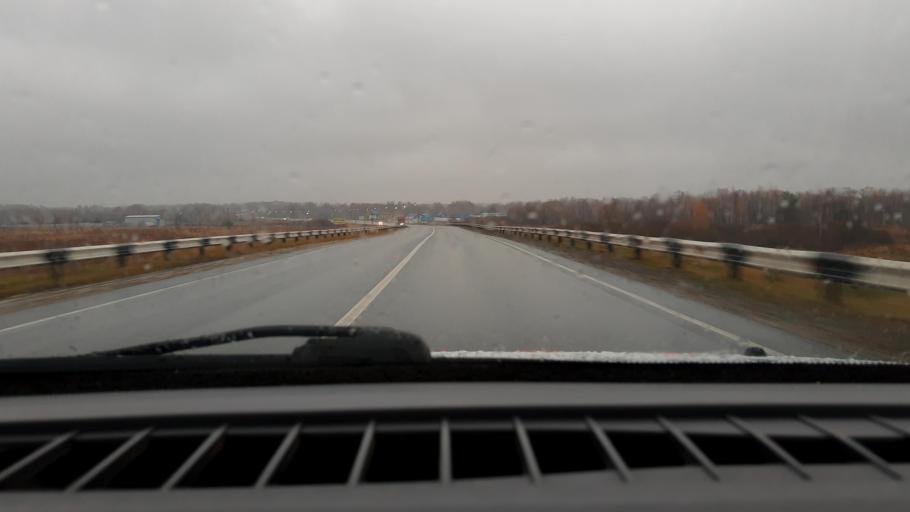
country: RU
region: Nizjnij Novgorod
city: Sitniki
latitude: 56.4958
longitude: 44.0244
